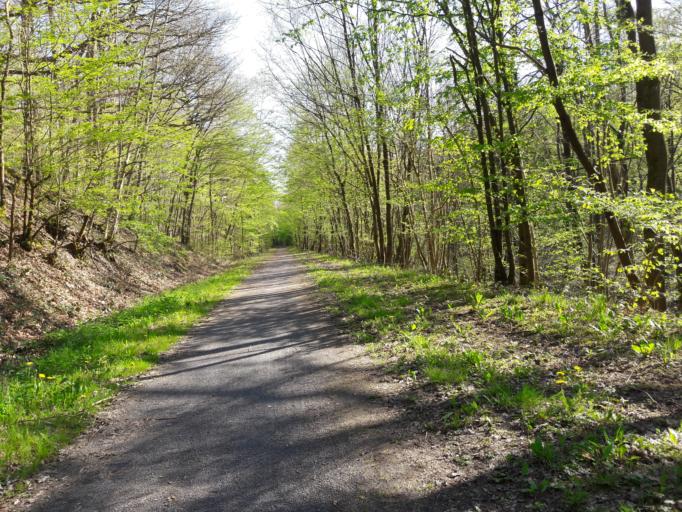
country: FR
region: Nord-Pas-de-Calais
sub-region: Departement du Nord
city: Sains-du-Nord
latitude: 50.1362
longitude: 4.0662
